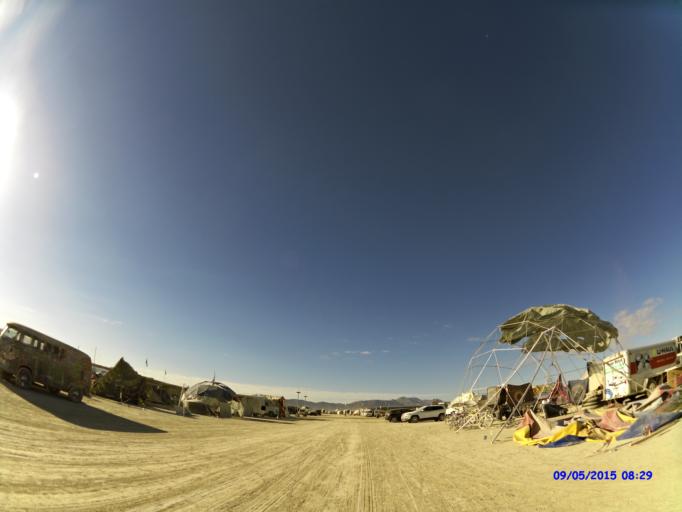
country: US
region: Nevada
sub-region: Pershing County
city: Lovelock
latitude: 40.7870
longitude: -119.2180
